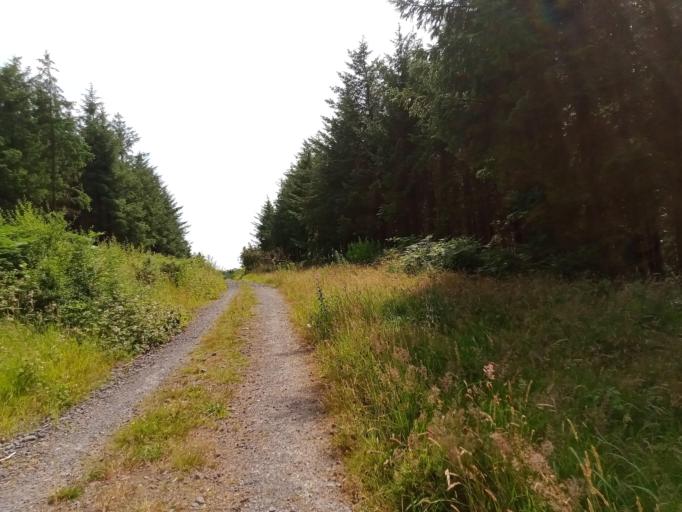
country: IE
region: Leinster
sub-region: Kilkenny
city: Ballyragget
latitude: 52.8028
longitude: -7.4543
